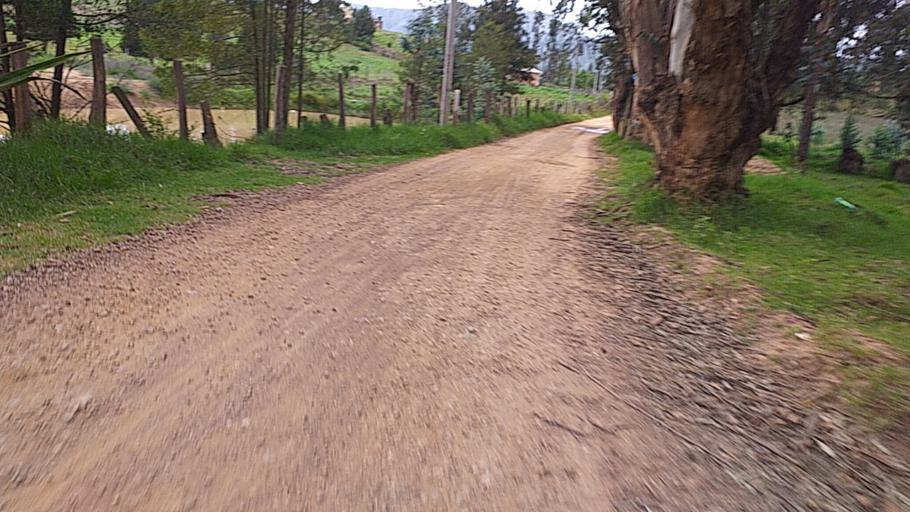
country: CO
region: Boyaca
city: Floresta
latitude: 5.8685
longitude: -72.9185
